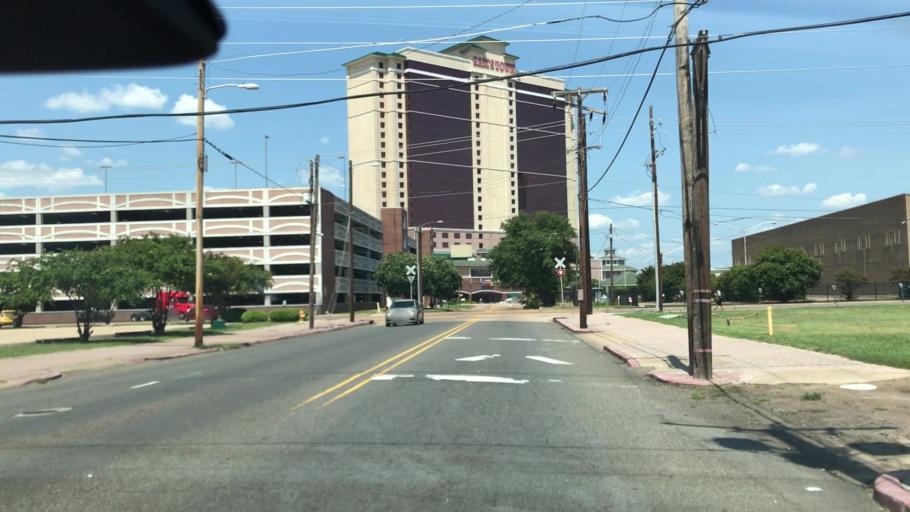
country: US
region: Louisiana
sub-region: Caddo Parish
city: Shreveport
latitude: 32.5169
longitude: -93.7480
